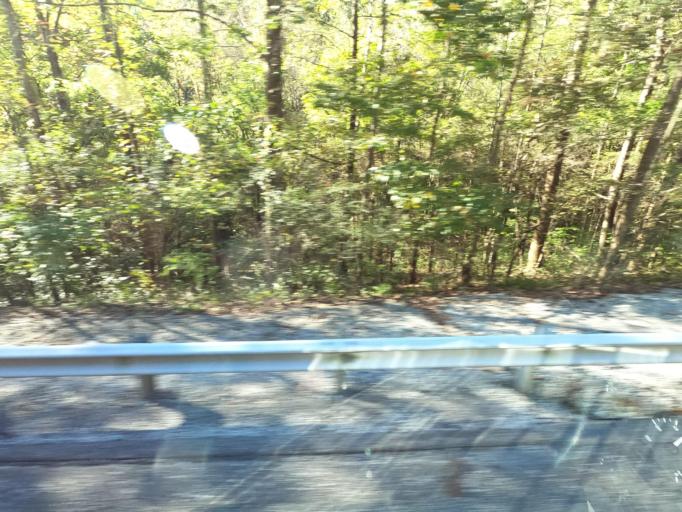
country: US
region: Tennessee
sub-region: Giles County
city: Pulaski
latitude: 35.1769
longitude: -86.8747
